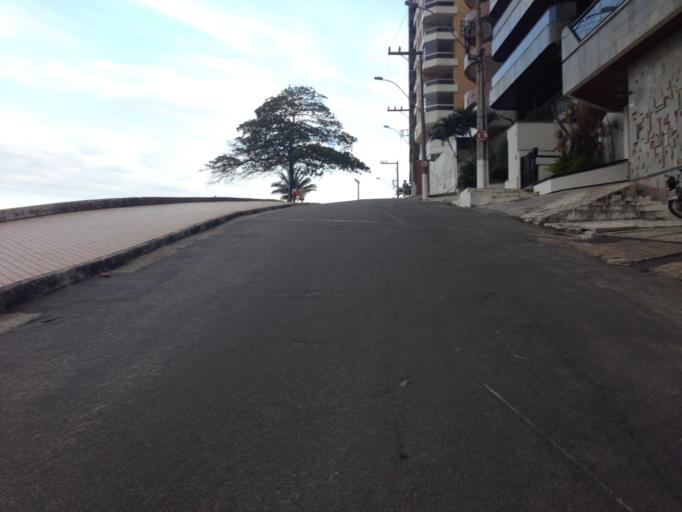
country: BR
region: Espirito Santo
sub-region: Guarapari
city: Guarapari
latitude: -20.6694
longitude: -40.4939
